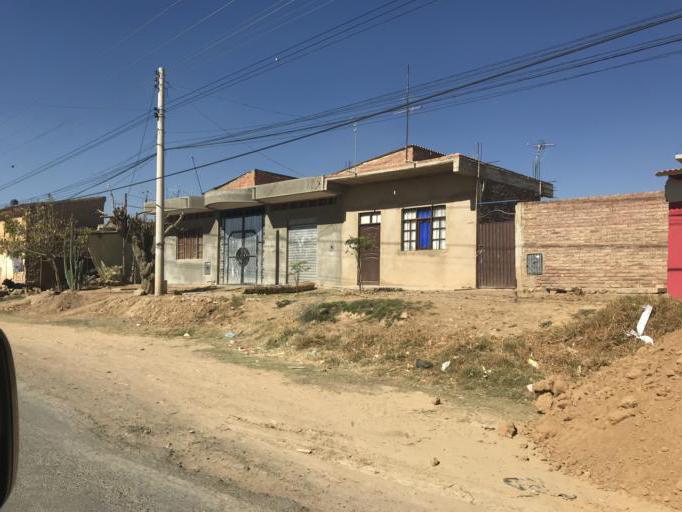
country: BO
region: Cochabamba
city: Cliza
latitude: -17.5761
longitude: -65.9052
